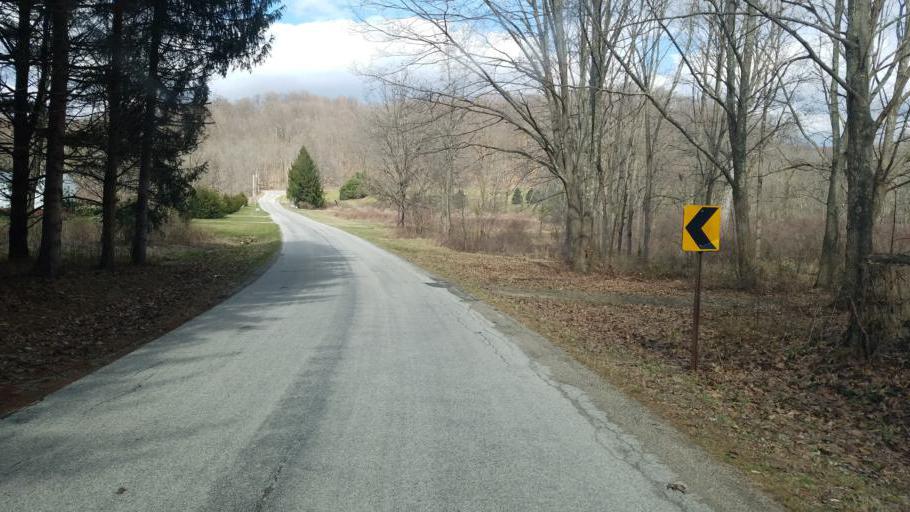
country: US
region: Ohio
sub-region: Sandusky County
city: Bellville
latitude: 40.6330
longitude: -82.4600
